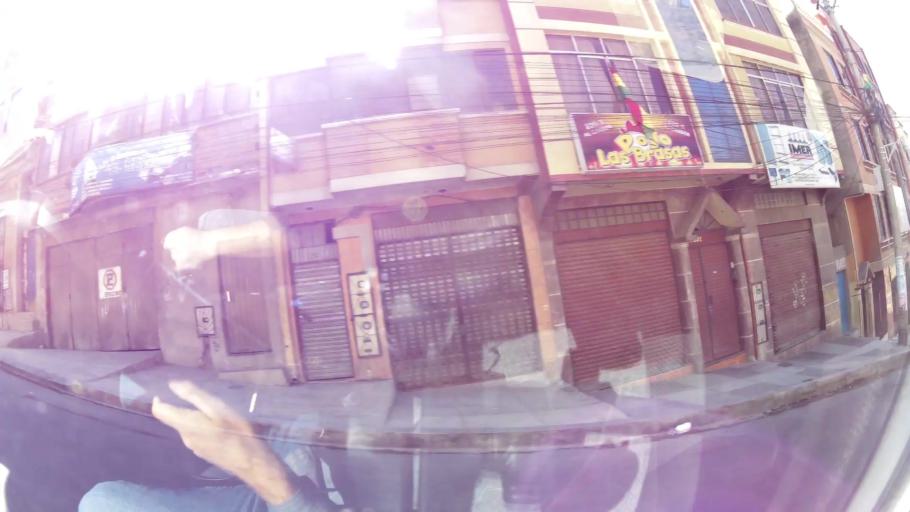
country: BO
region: La Paz
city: La Paz
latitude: -16.4935
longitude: -68.1491
